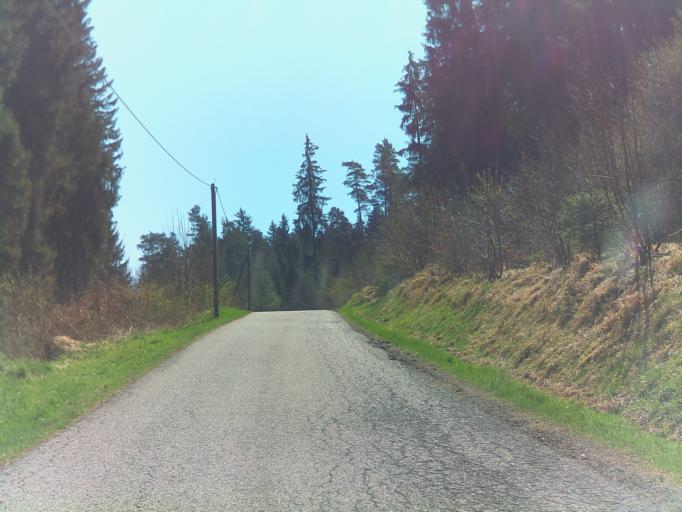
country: DE
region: Bavaria
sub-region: Upper Palatinate
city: Kastl
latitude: 49.3843
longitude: 11.6902
